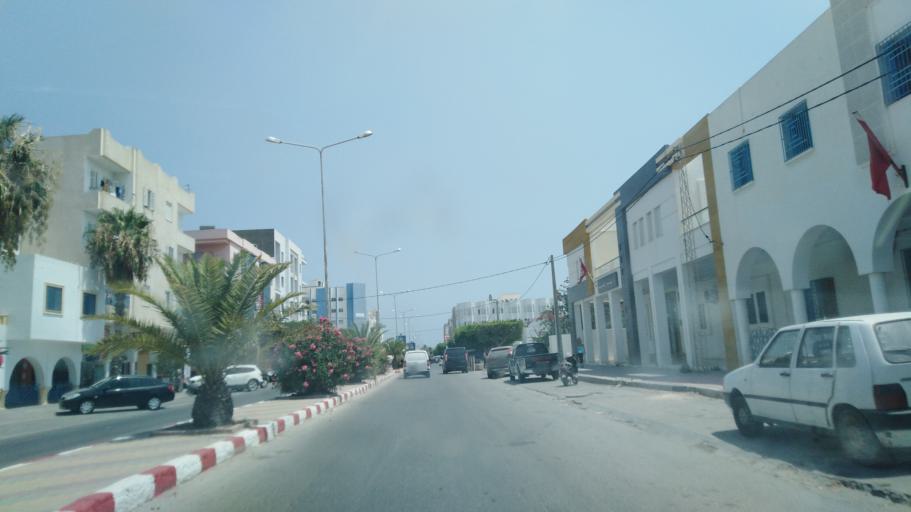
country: TN
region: Al Mahdiyah
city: Mahdia
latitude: 35.5079
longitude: 11.0508
